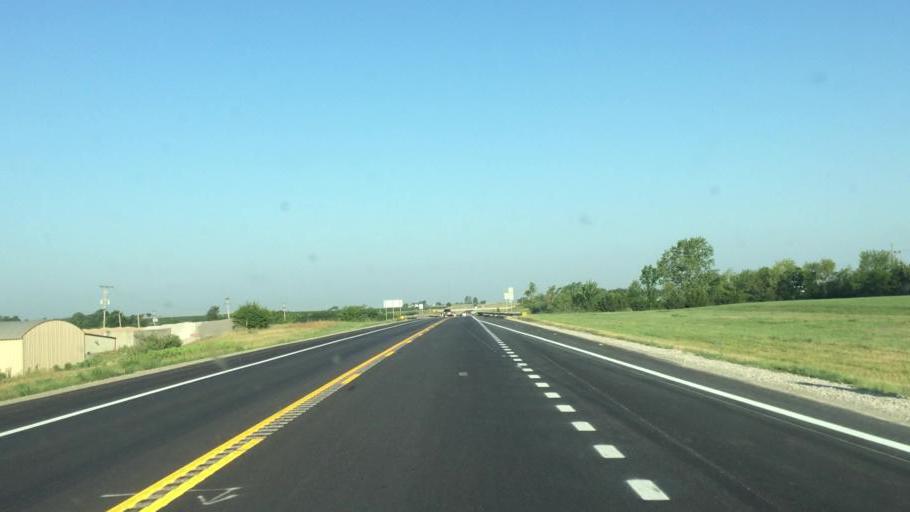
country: US
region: Kansas
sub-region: Brown County
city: Hiawatha
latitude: 39.8407
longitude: -95.5341
